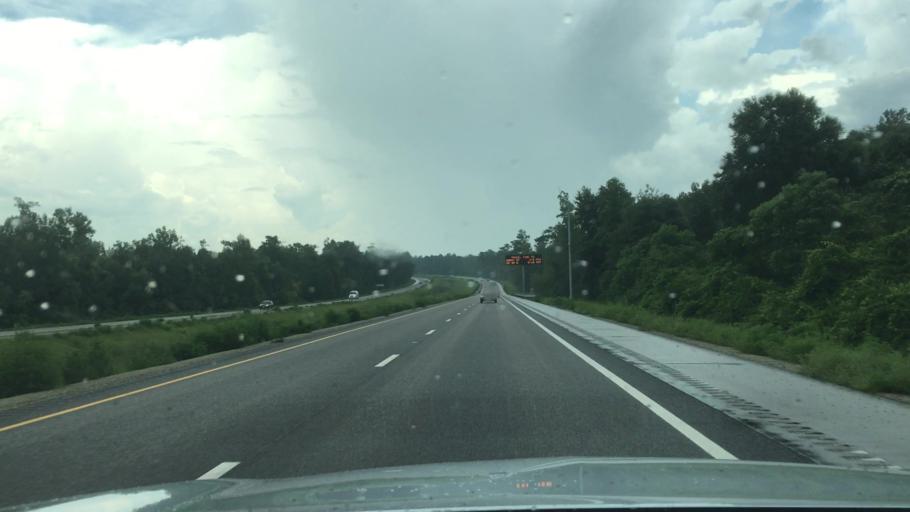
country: US
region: Mississippi
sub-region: Lamar County
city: West Hattiesburg
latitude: 31.2196
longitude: -89.3272
